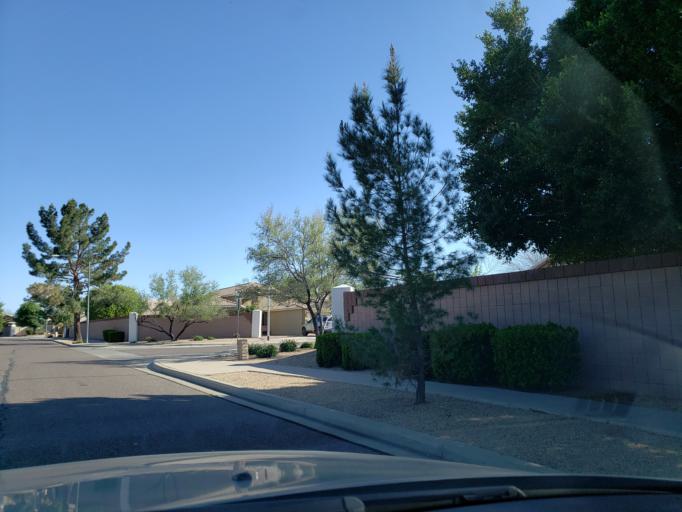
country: US
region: Arizona
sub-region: Maricopa County
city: Glendale
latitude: 33.5498
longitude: -112.1714
